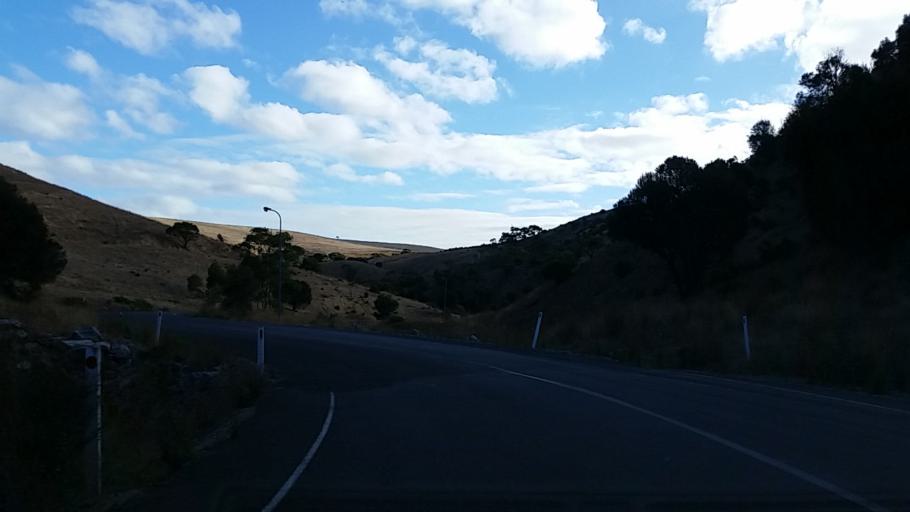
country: AU
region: South Australia
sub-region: Yankalilla
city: Normanville
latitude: -35.5028
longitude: 138.2466
